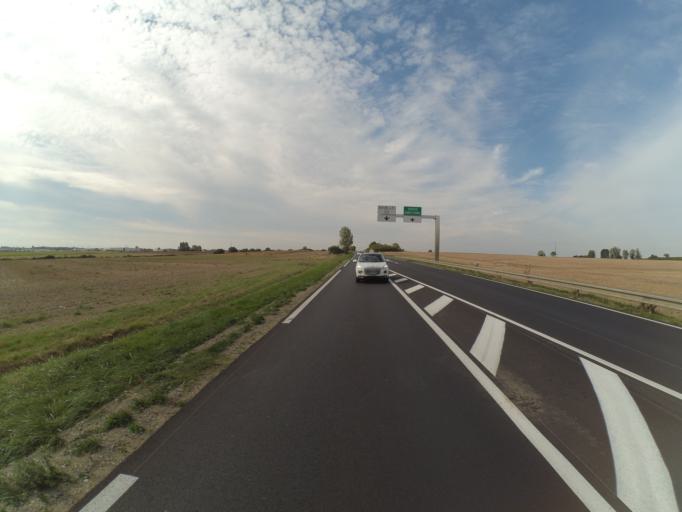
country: FR
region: Pays de la Loire
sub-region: Departement de Maine-et-Loire
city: Doue-la-Fontaine
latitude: 47.1978
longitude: -0.2390
